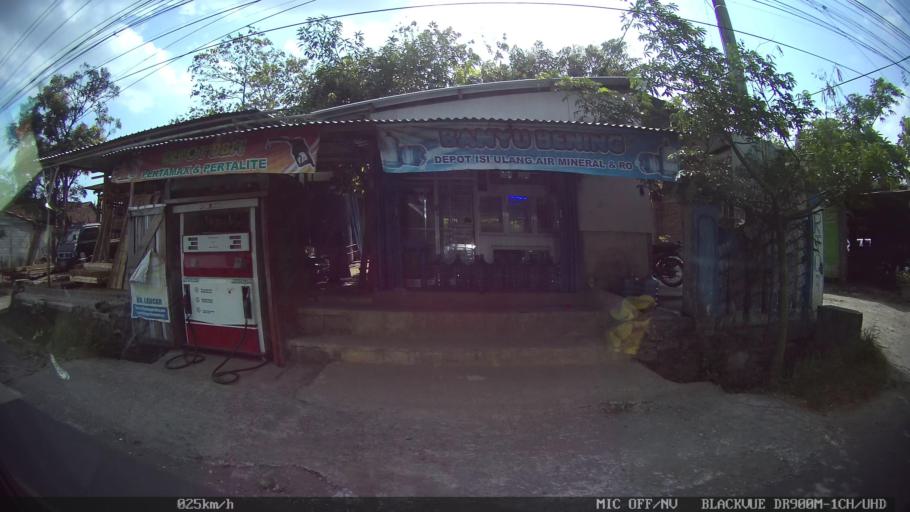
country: ID
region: Daerah Istimewa Yogyakarta
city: Kasihan
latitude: -7.8347
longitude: 110.3132
